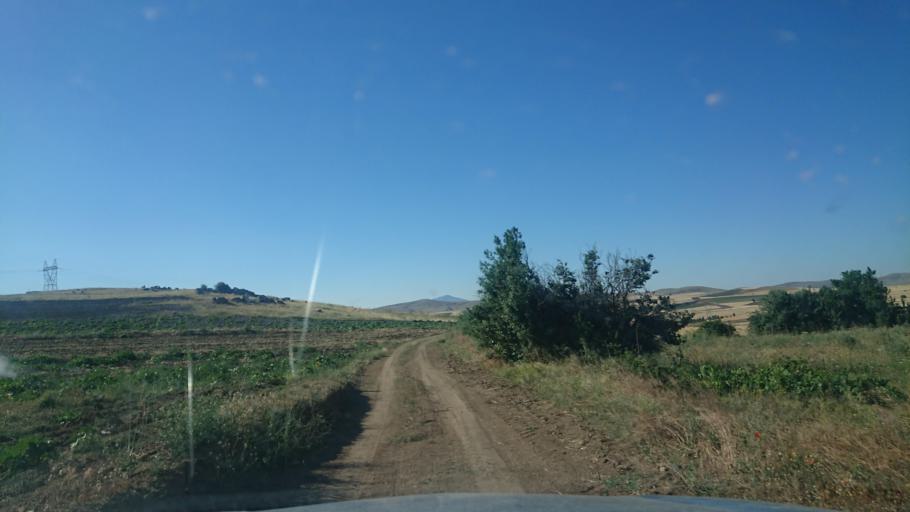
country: TR
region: Aksaray
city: Agacoren
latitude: 38.8325
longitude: 33.9422
